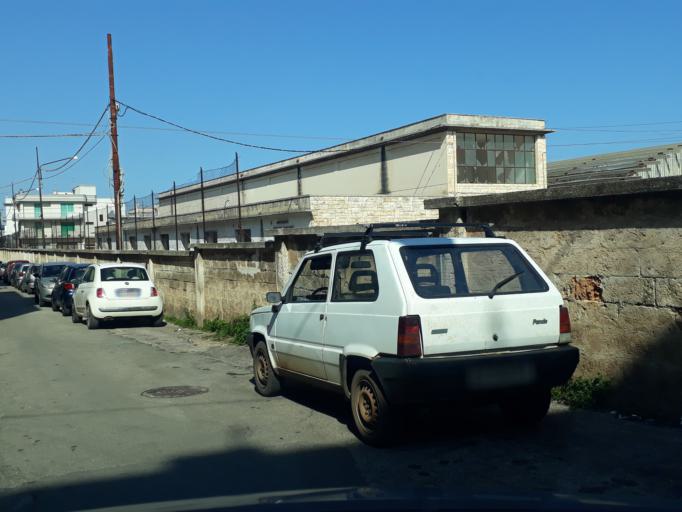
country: IT
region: Apulia
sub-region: Provincia di Brindisi
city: Fasano
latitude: 40.8384
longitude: 17.3624
